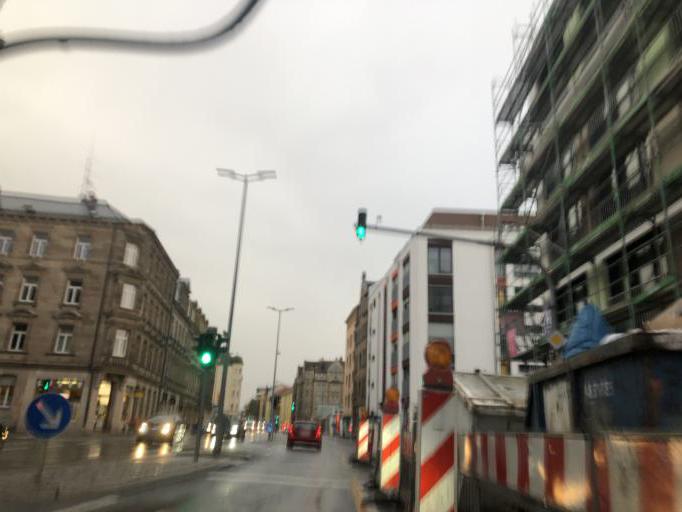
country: DE
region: Bavaria
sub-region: Regierungsbezirk Mittelfranken
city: Furth
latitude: 49.4651
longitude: 10.9858
